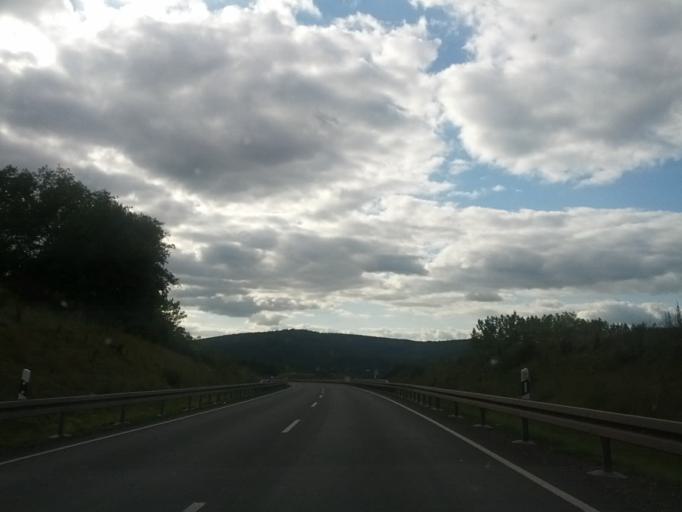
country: DE
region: Thuringia
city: Fambach
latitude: 50.7125
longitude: 10.3848
